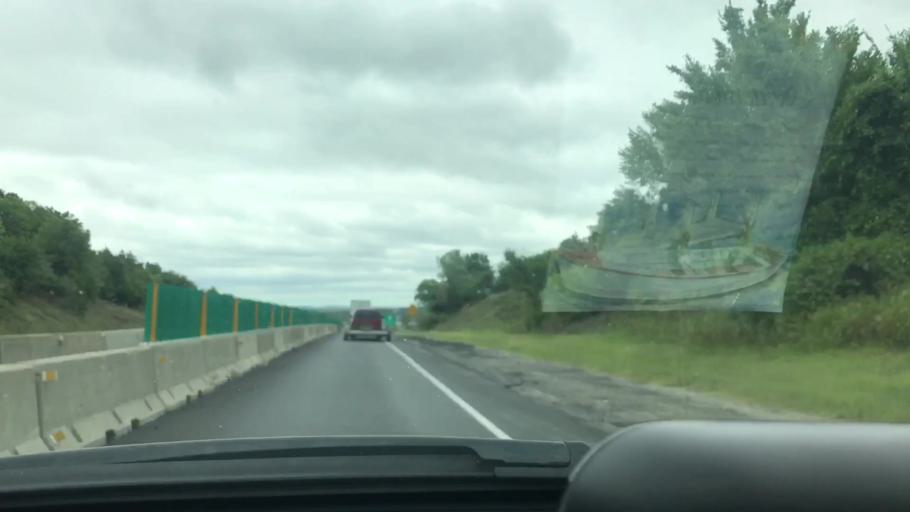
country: US
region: Oklahoma
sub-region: McIntosh County
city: Eufaula
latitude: 35.2894
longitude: -95.5931
